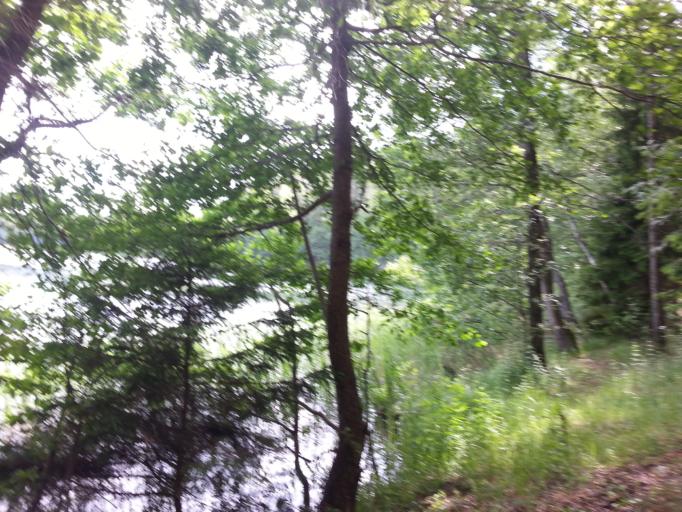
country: BY
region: Vitebsk
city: Lyntupy
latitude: 54.9654
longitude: 26.3781
